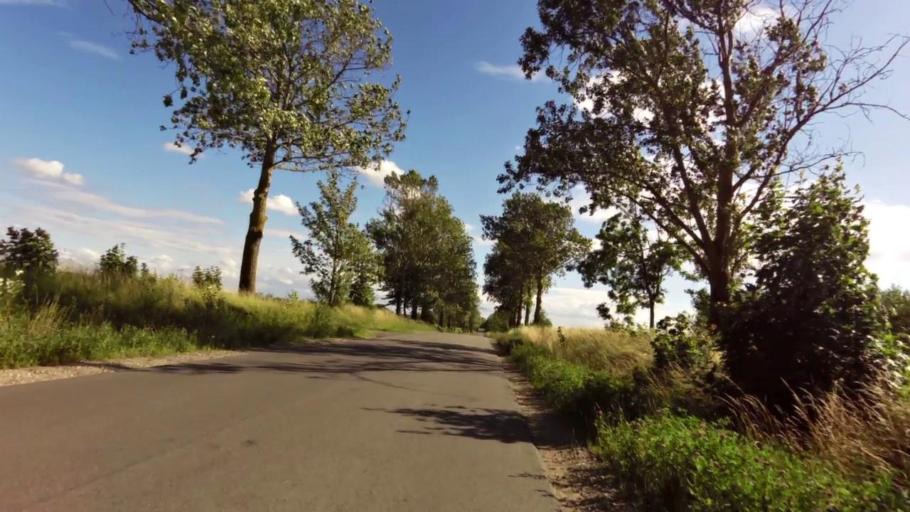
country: PL
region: West Pomeranian Voivodeship
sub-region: Powiat slawienski
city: Slawno
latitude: 54.4431
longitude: 16.7348
